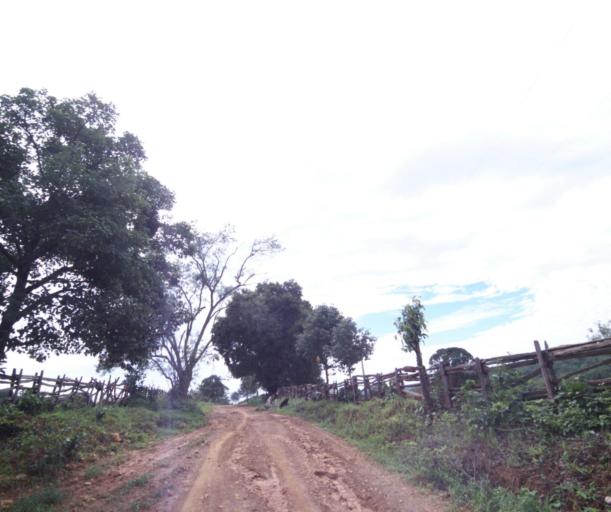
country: BR
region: Bahia
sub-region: Carinhanha
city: Carinhanha
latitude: -14.2393
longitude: -44.3980
